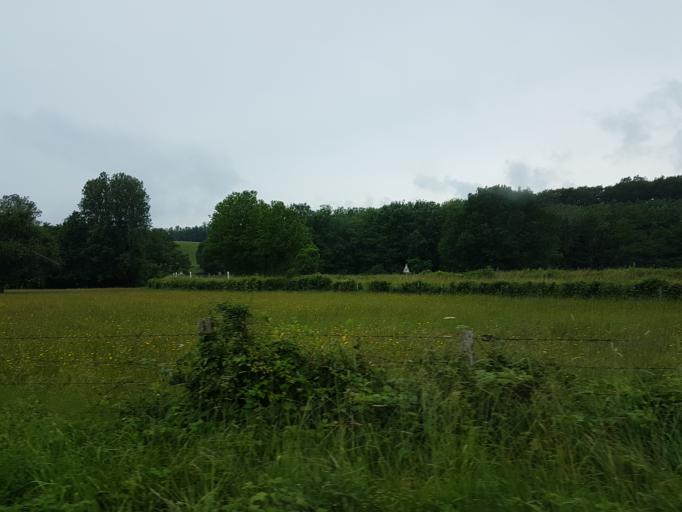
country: FR
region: Bourgogne
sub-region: Departement de la Nievre
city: Corbigny
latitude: 47.1853
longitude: 3.7352
